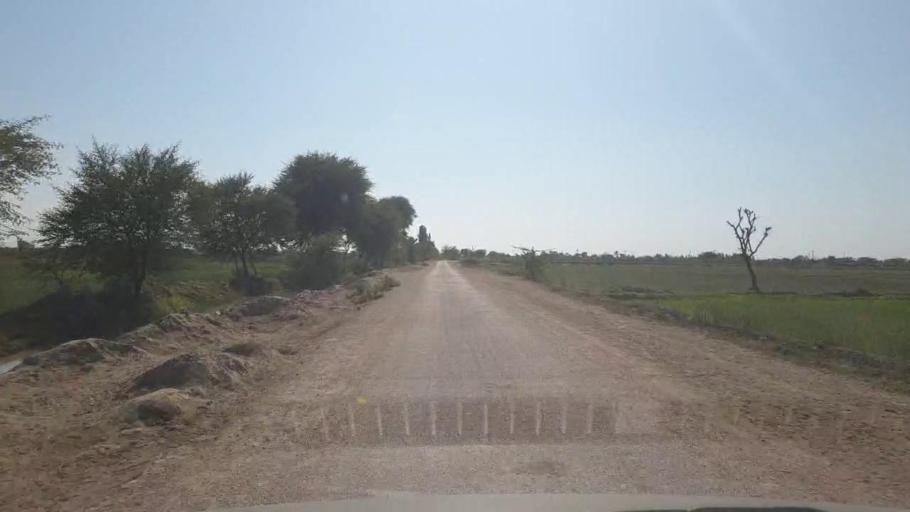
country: PK
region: Sindh
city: Dhoro Naro
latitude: 25.4012
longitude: 69.5962
